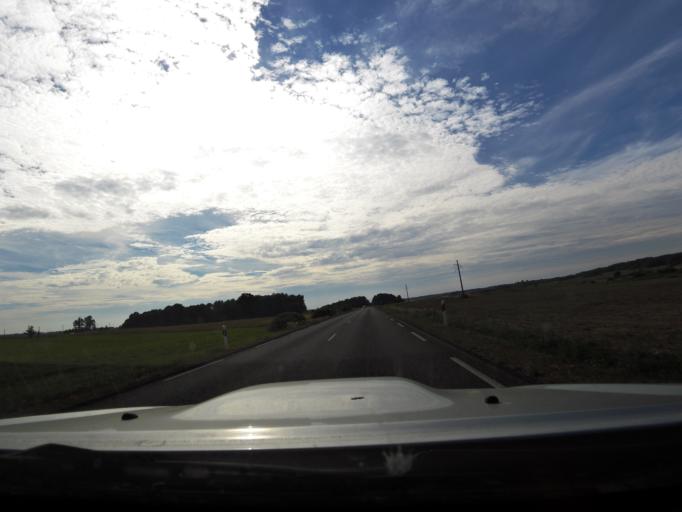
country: LT
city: Grigiskes
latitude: 54.8673
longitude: 25.0375
